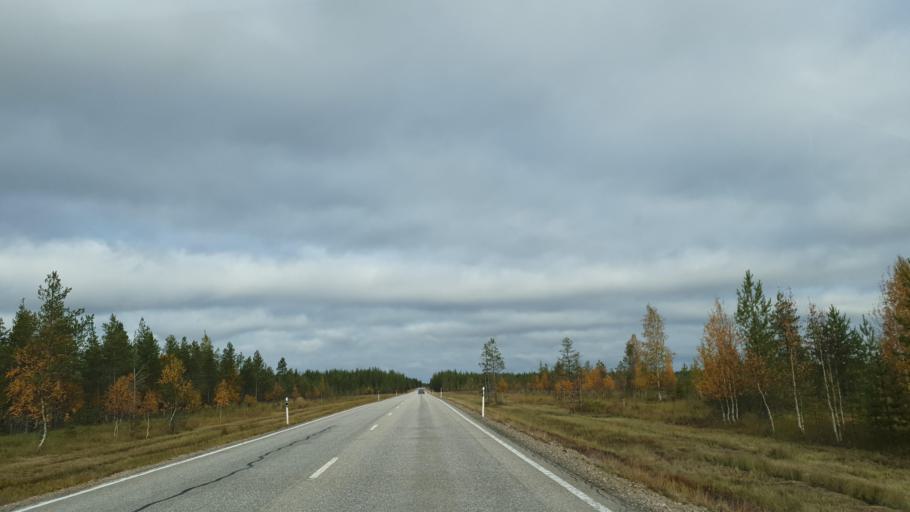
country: FI
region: Northern Ostrobothnia
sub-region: Oulunkaari
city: Pudasjaervi
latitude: 65.5821
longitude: 26.7341
